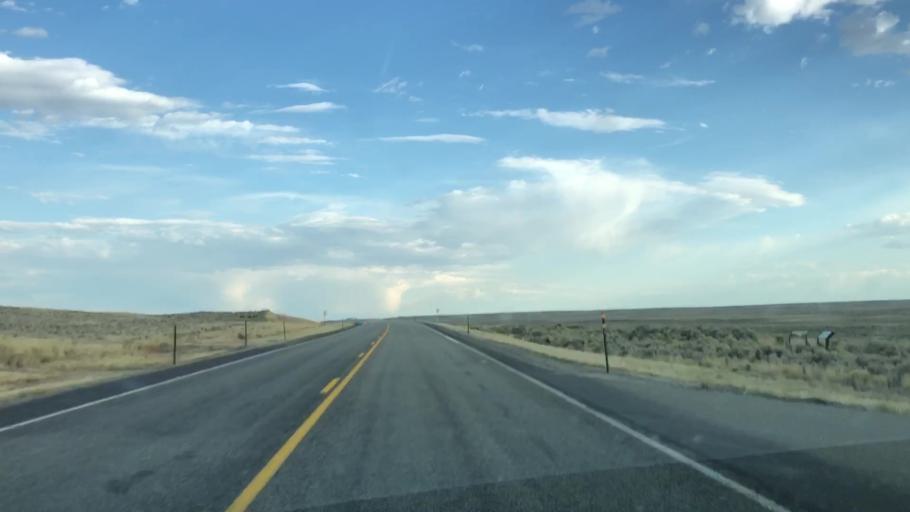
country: US
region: Wyoming
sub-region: Sublette County
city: Pinedale
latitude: 42.6258
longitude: -109.6581
